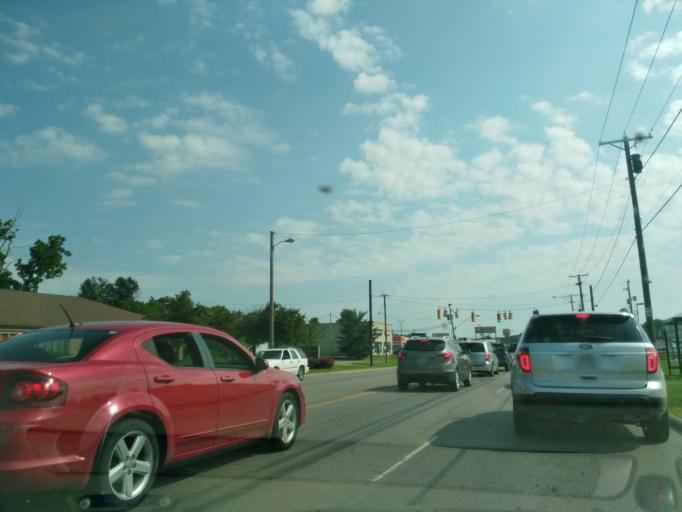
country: US
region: Ohio
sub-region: Muskingum County
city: South Zanesville
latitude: 39.9091
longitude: -82.0171
